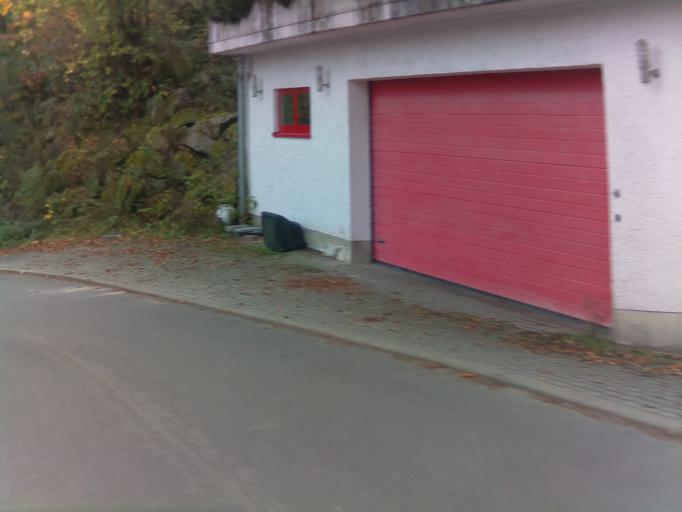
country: DE
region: Hesse
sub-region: Regierungsbezirk Darmstadt
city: Birkenau
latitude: 49.5292
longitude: 8.7247
